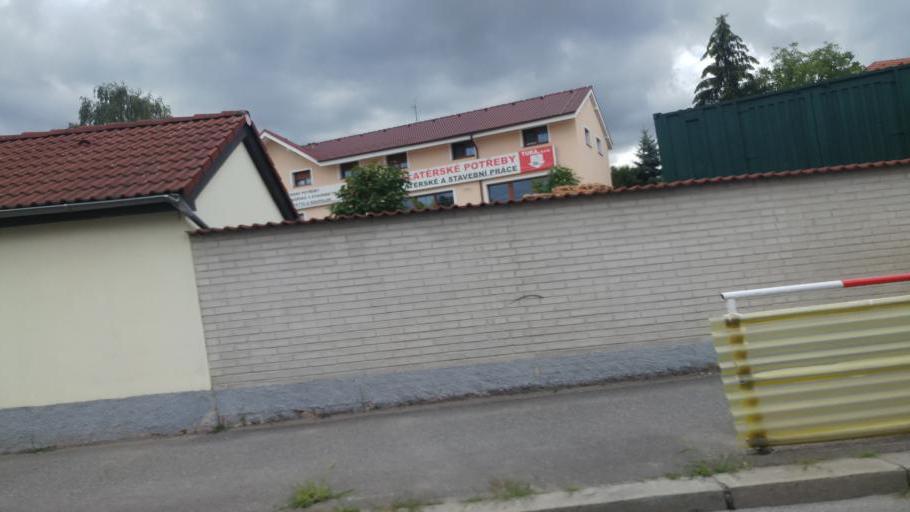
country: CZ
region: Praha
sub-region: Praha 9
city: Vysocany
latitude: 50.0862
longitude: 14.5130
